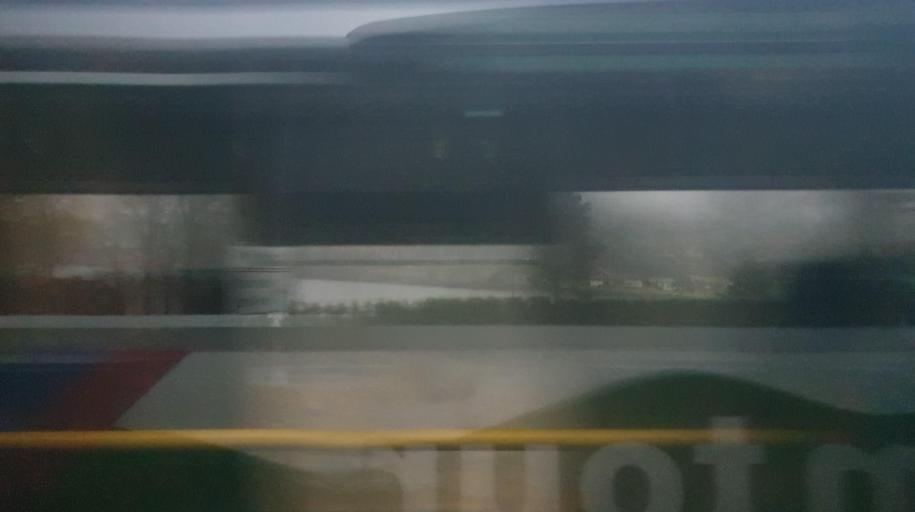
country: NO
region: Buskerud
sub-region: Krodsherad
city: Noresund
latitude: 60.1846
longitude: 9.6151
